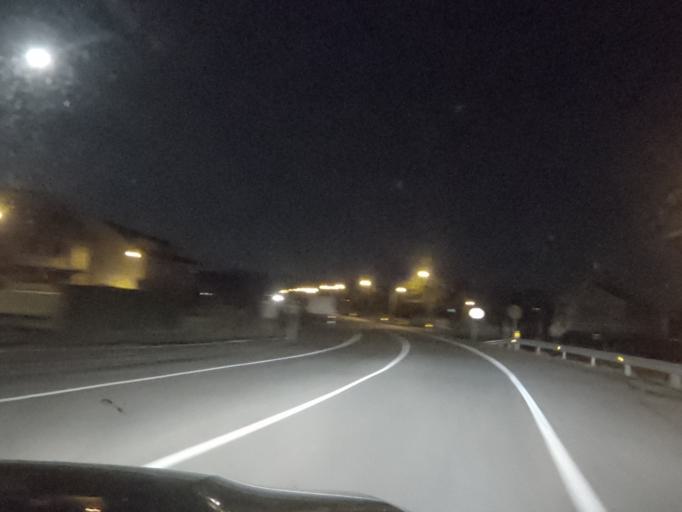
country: ES
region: Galicia
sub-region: Provincia de Ourense
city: Verin
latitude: 41.9472
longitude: -7.4886
